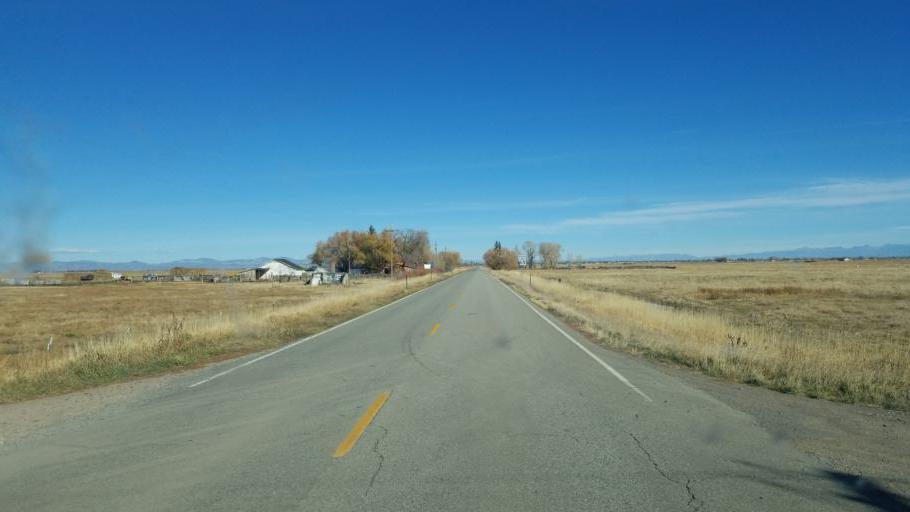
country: US
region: Colorado
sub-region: Rio Grande County
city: Monte Vista
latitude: 37.5240
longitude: -106.1493
